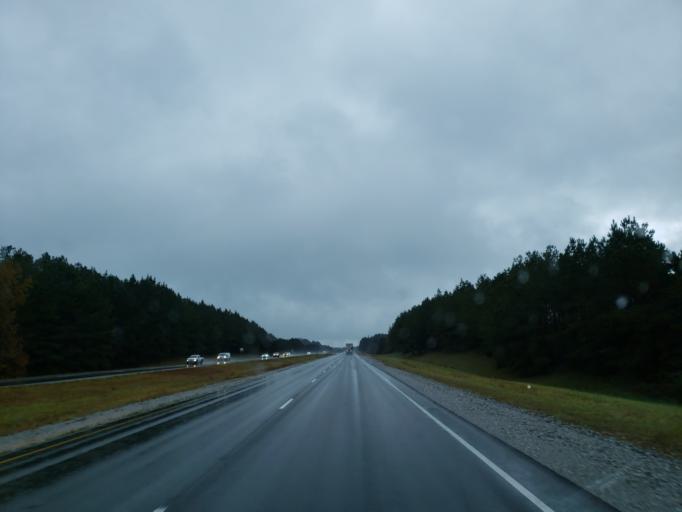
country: US
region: Mississippi
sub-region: Clarke County
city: Stonewall
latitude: 32.1867
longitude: -88.7086
